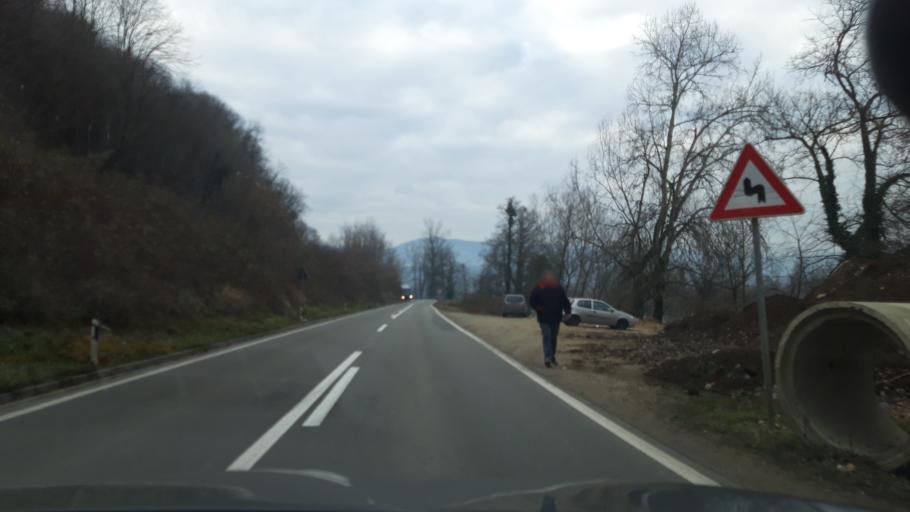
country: BA
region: Republika Srpska
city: Zvornik
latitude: 44.4194
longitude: 19.1486
